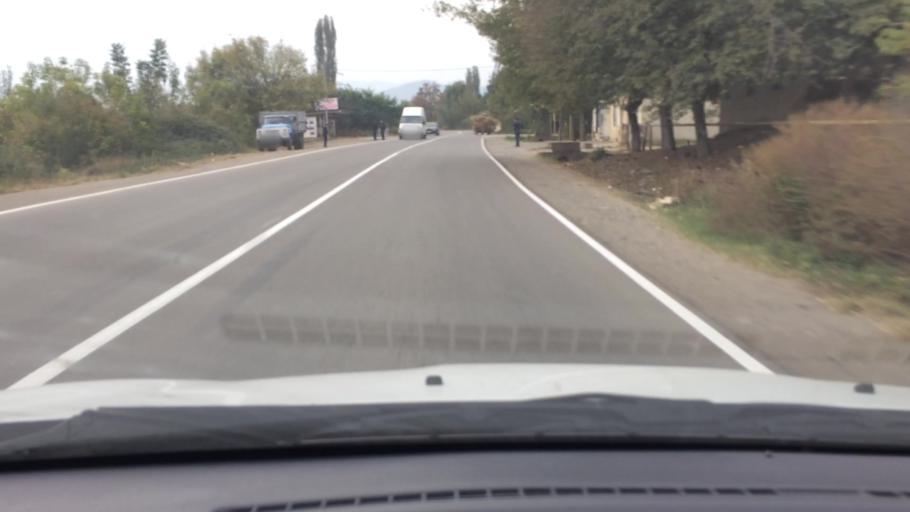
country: GE
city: Naghvarevi
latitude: 41.3265
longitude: 44.8011
